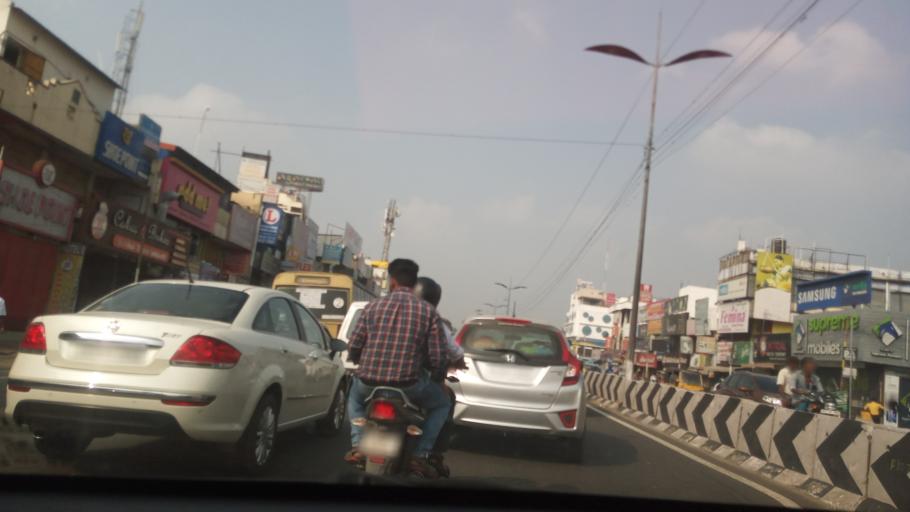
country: IN
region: Tamil Nadu
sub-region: Coimbatore
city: Singanallur
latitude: 11.0262
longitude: 77.0196
